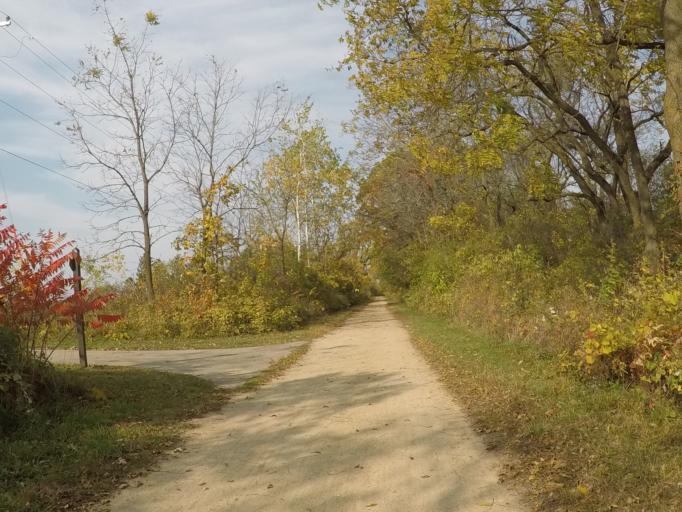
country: US
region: Wisconsin
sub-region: Iowa County
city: Barneveld
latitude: 43.0141
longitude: -89.8217
